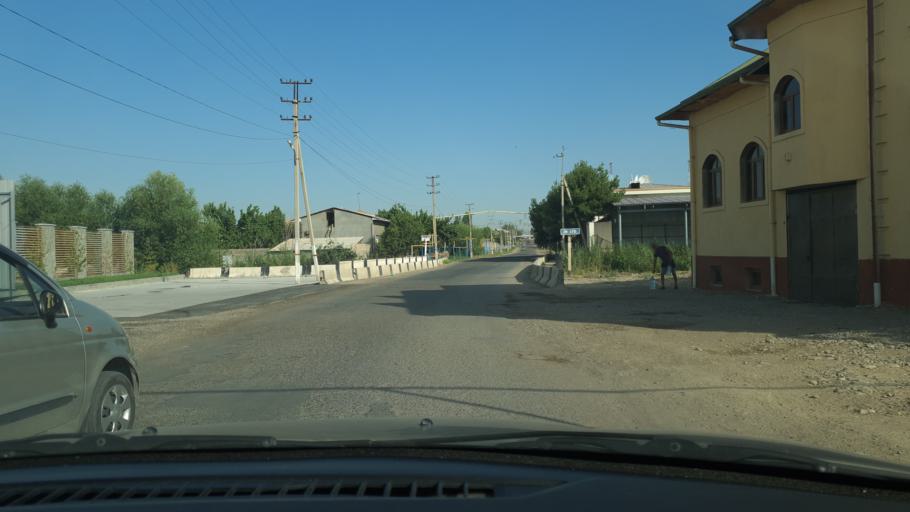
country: UZ
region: Toshkent
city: Urtaowul
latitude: 41.2035
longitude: 69.1524
